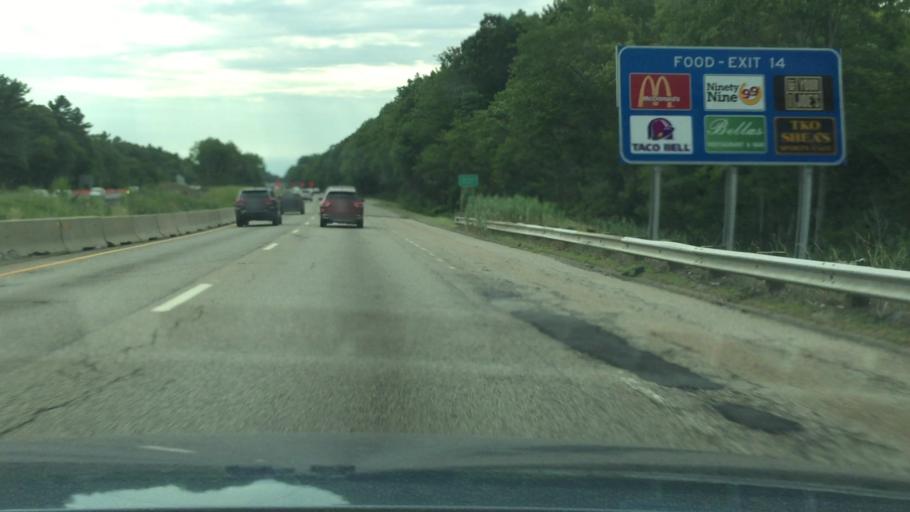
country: US
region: Massachusetts
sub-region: Plymouth County
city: Rockland
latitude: 42.1566
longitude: -70.8597
